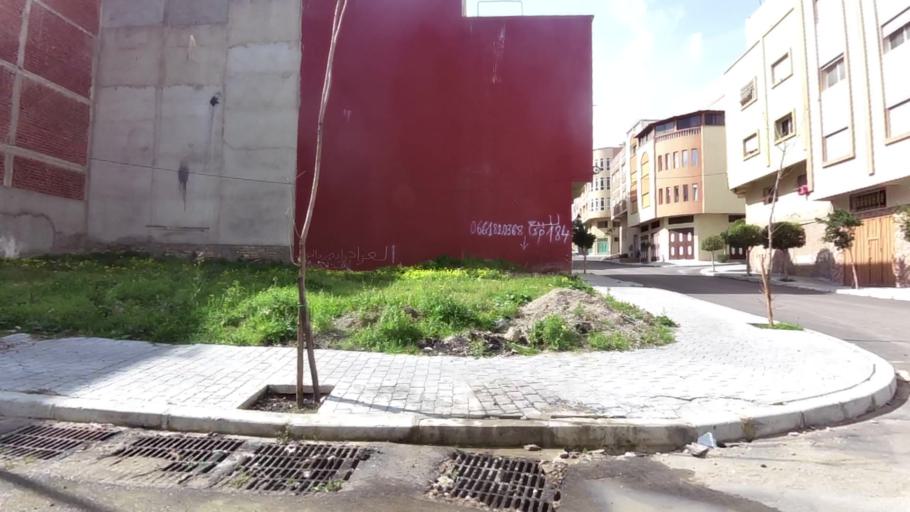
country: MA
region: Tanger-Tetouan
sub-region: Tanger-Assilah
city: Tangier
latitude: 35.7683
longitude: -5.7634
